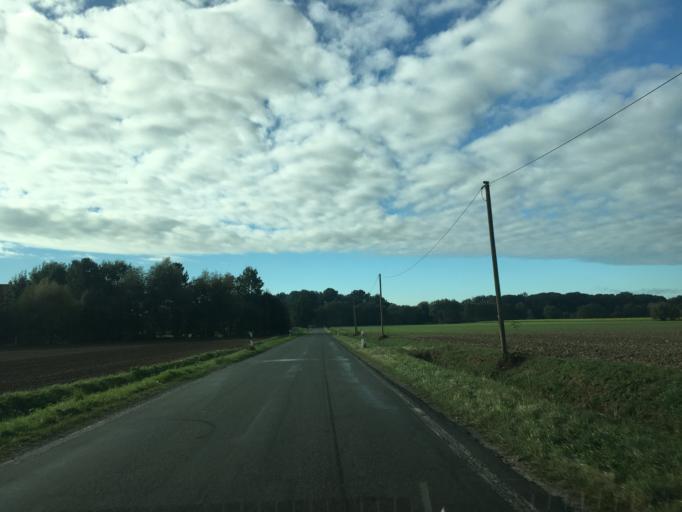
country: DE
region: North Rhine-Westphalia
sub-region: Regierungsbezirk Munster
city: Havixbeck
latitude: 51.9826
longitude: 7.4725
